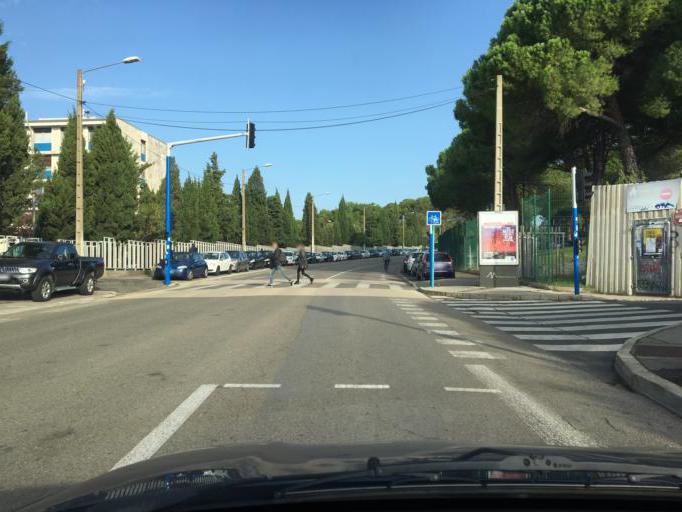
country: FR
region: Languedoc-Roussillon
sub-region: Departement de l'Herault
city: Montpellier
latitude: 43.6320
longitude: 3.8685
